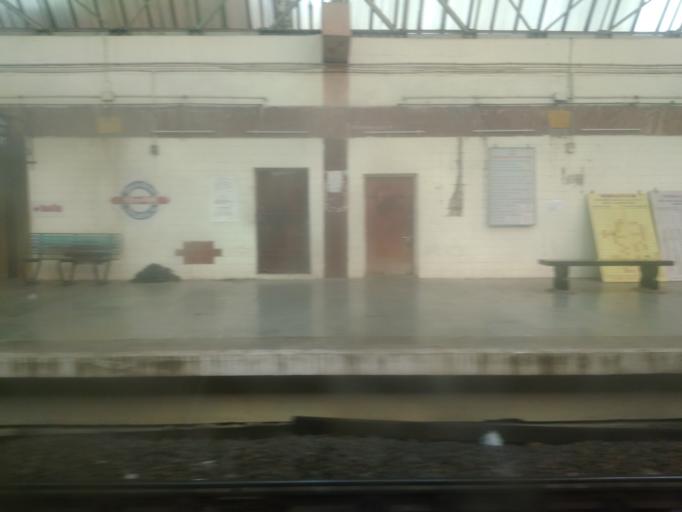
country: IN
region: Tamil Nadu
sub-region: Chennai
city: Gandhi Nagar
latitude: 13.0346
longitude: 80.2669
